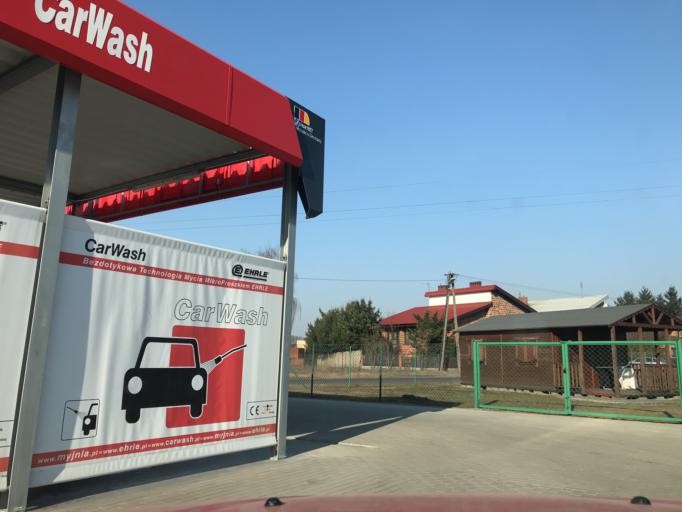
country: PL
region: Greater Poland Voivodeship
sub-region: Powiat sredzki
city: Nowe Miasto nad Warta
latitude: 52.0837
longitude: 17.4025
